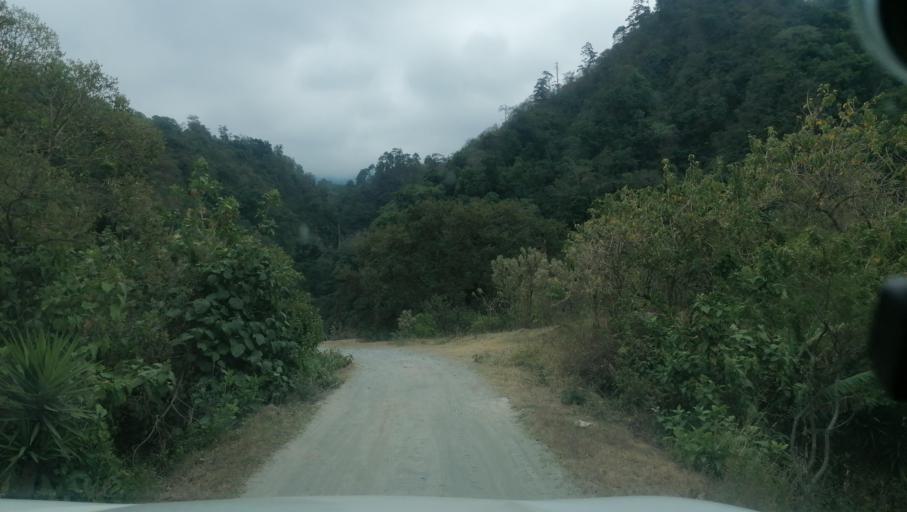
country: MX
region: Chiapas
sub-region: Cacahoatan
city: Benito Juarez
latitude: 15.1674
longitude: -92.1676
